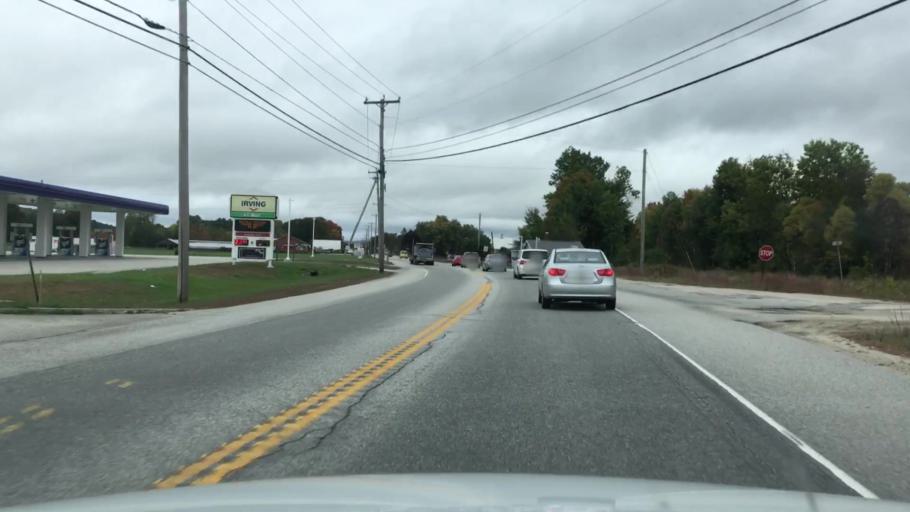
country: US
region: Maine
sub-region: Oxford County
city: South Paris
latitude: 44.1805
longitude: -70.5157
